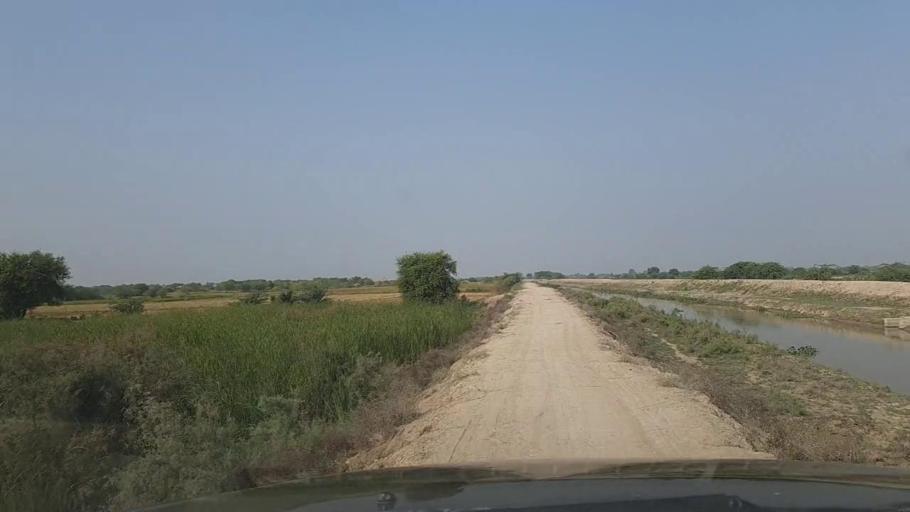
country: PK
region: Sindh
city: Mirpur Batoro
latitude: 24.6829
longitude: 68.2482
